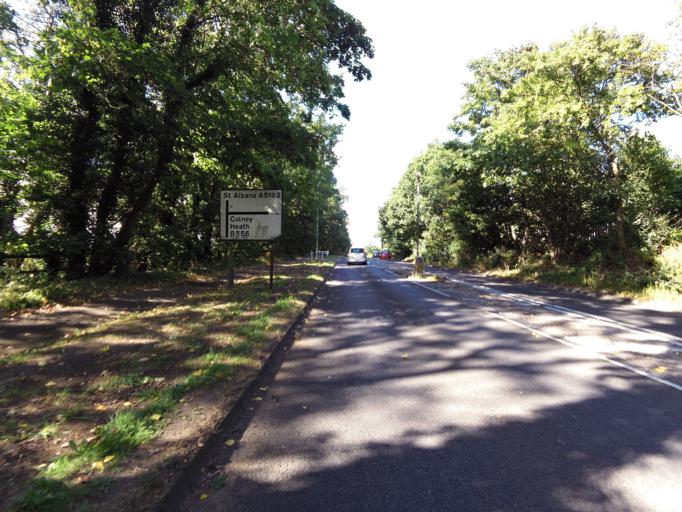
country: GB
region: England
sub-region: Hertfordshire
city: Radlett
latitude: 51.6970
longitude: -0.3247
